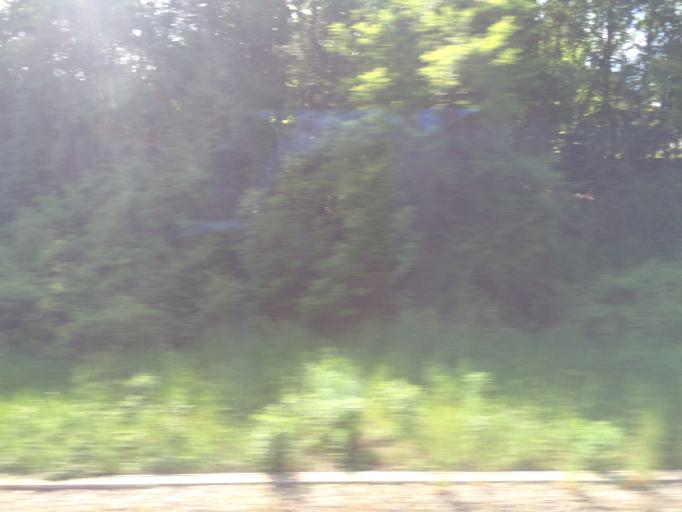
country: DE
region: Bavaria
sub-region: Regierungsbezirk Unterfranken
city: Kitzingen
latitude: 49.7437
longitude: 10.1583
